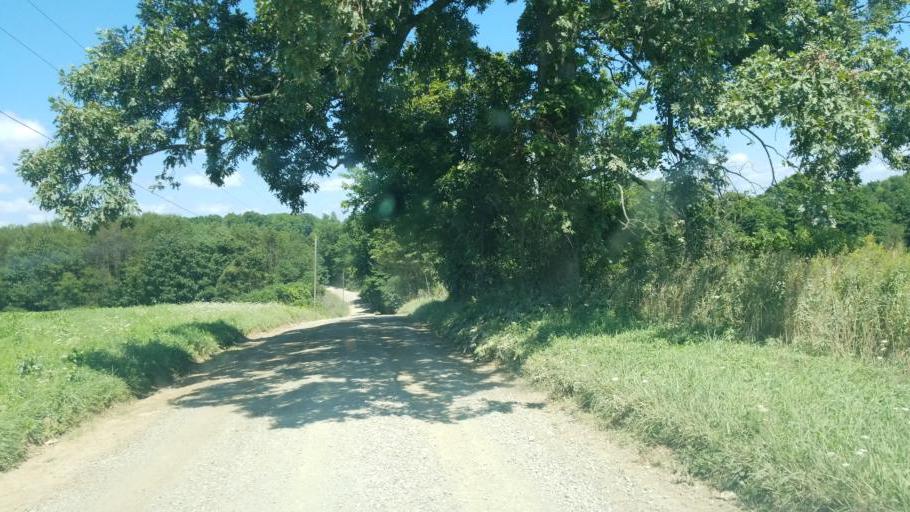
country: US
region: Pennsylvania
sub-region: Clarion County
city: Knox
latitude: 41.2064
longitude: -79.5276
